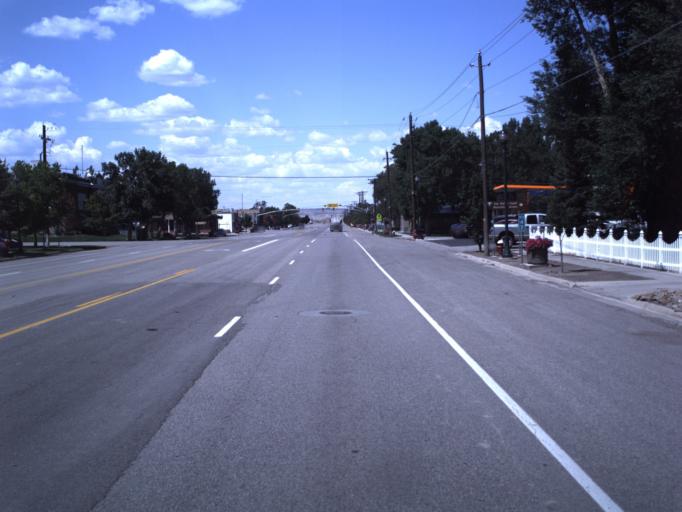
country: US
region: Utah
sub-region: Emery County
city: Huntington
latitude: 39.3255
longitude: -110.9645
